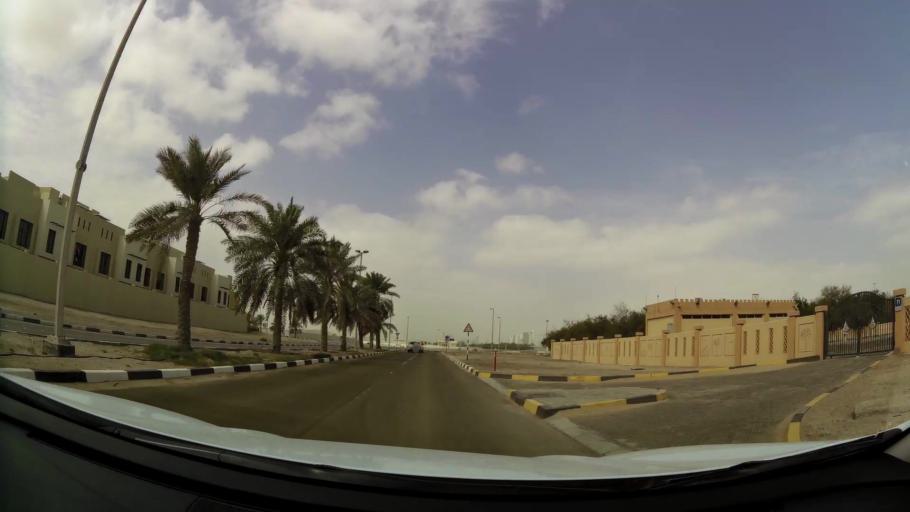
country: AE
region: Abu Dhabi
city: Abu Dhabi
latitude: 24.4010
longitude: 54.4889
